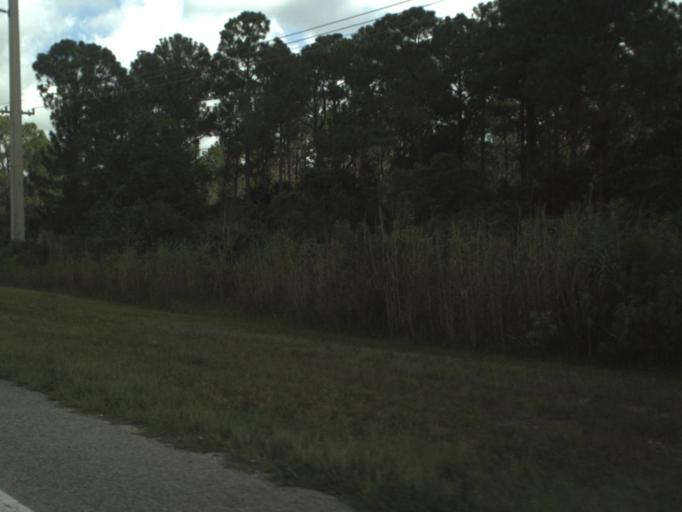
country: US
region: Florida
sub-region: Palm Beach County
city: Limestone Creek
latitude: 26.8954
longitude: -80.2800
